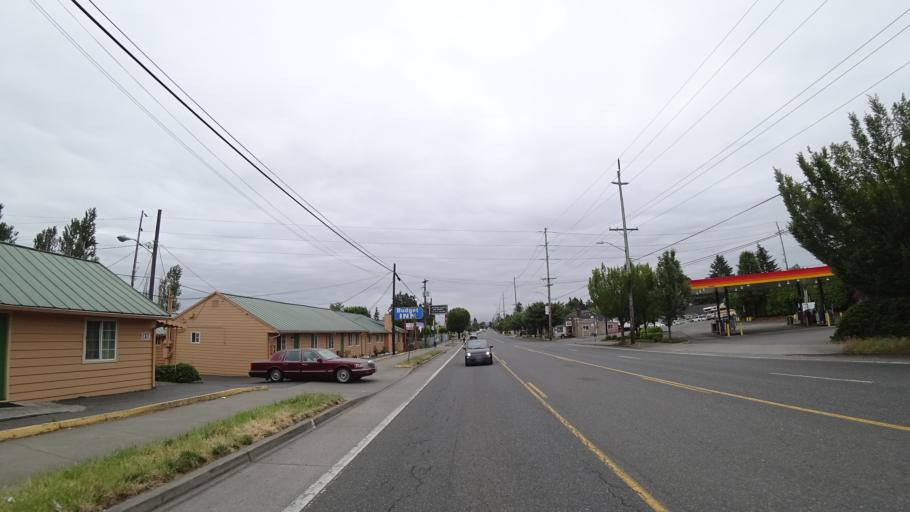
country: US
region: Oregon
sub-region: Multnomah County
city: Lents
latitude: 45.5580
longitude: -122.5449
